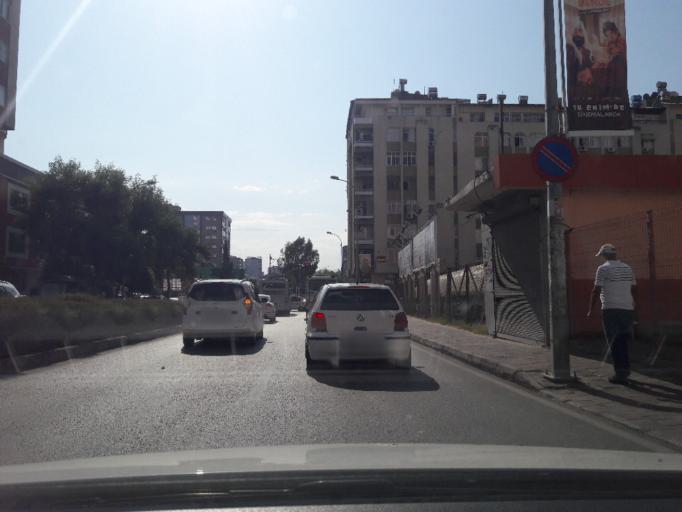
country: TR
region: Adana
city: Adana
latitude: 37.0080
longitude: 35.3242
